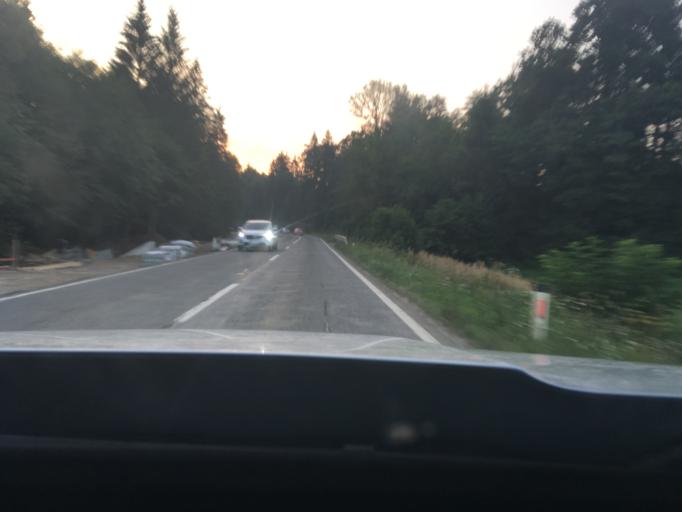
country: SI
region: Kocevje
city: Kocevje
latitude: 45.6803
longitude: 14.8228
